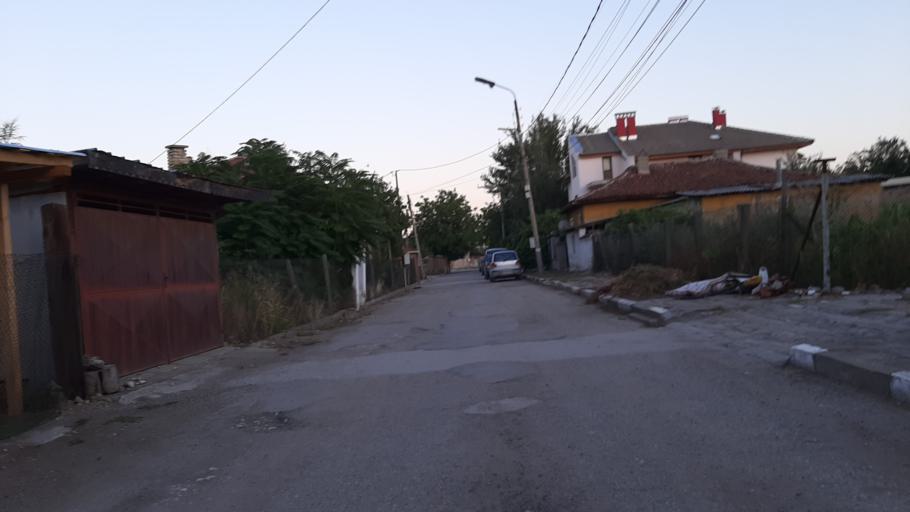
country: BG
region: Stara Zagora
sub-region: Obshtina Chirpan
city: Chirpan
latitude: 42.1067
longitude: 25.2185
